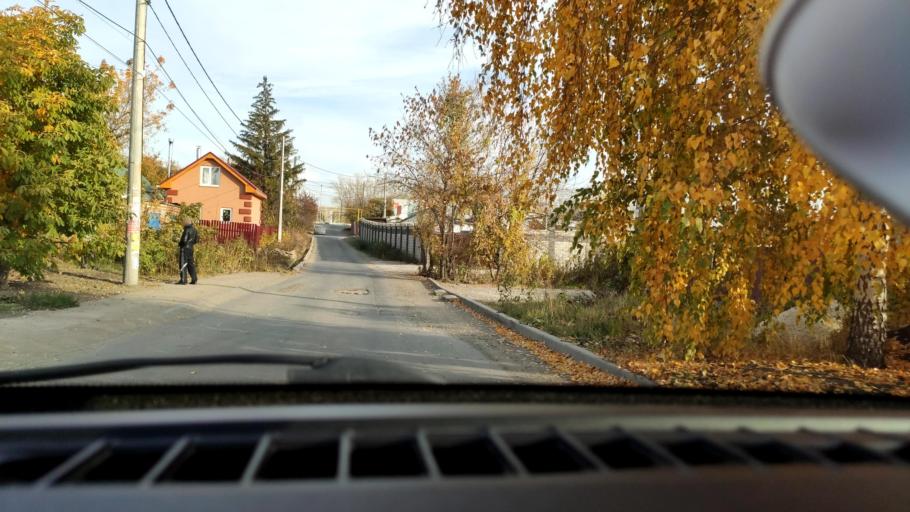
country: RU
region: Samara
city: Petra-Dubrava
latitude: 53.2934
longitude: 50.2826
